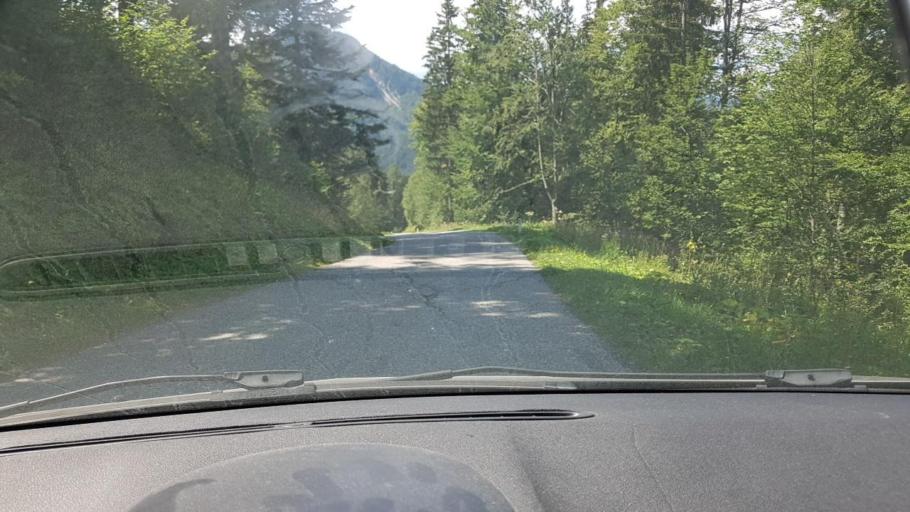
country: SI
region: Jezersko
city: Zgornje Jezersko
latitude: 46.4179
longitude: 14.5684
